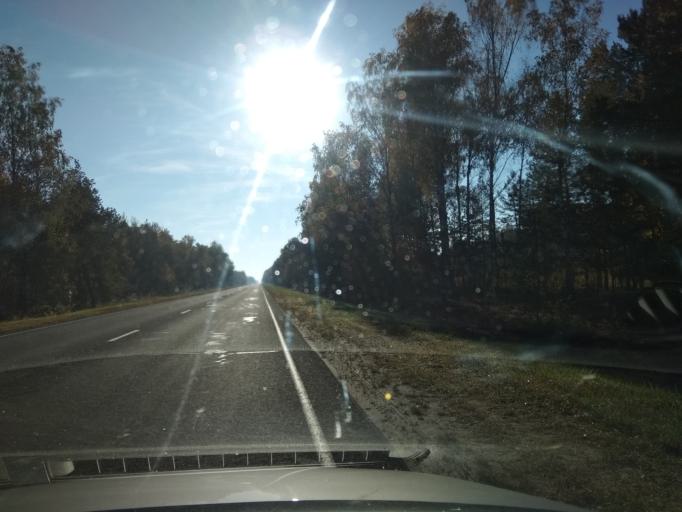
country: BY
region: Brest
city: Malaryta
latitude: 51.8859
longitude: 24.1521
